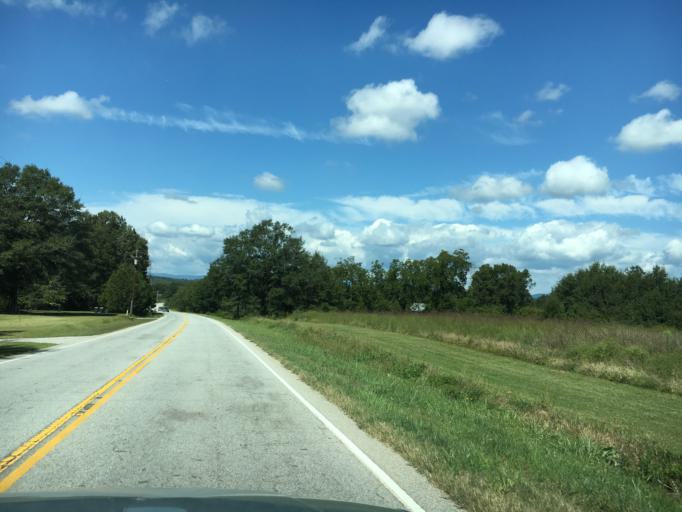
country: US
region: South Carolina
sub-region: Greenville County
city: Tigerville
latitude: 34.9971
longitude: -82.3499
